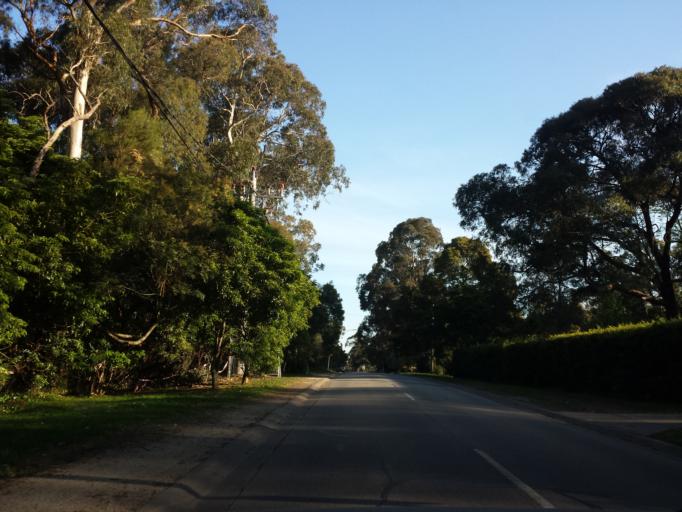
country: AU
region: Victoria
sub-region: Yarra Ranges
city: Belgrave
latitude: -37.9013
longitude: 145.3518
